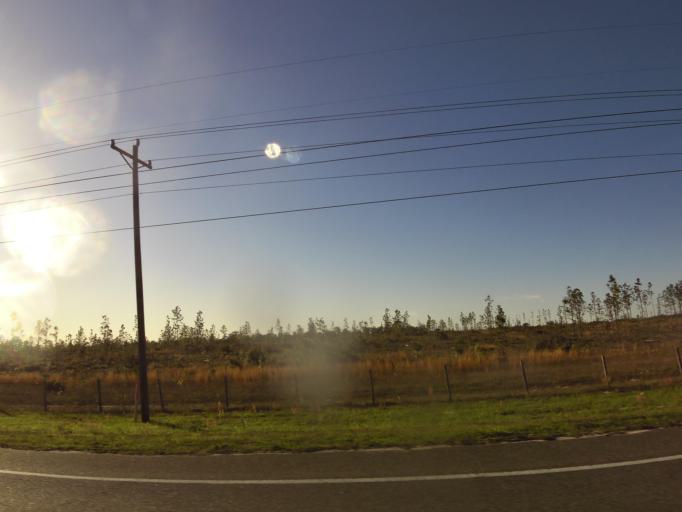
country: US
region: Florida
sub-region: Clay County
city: Keystone Heights
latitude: 29.8421
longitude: -81.9691
